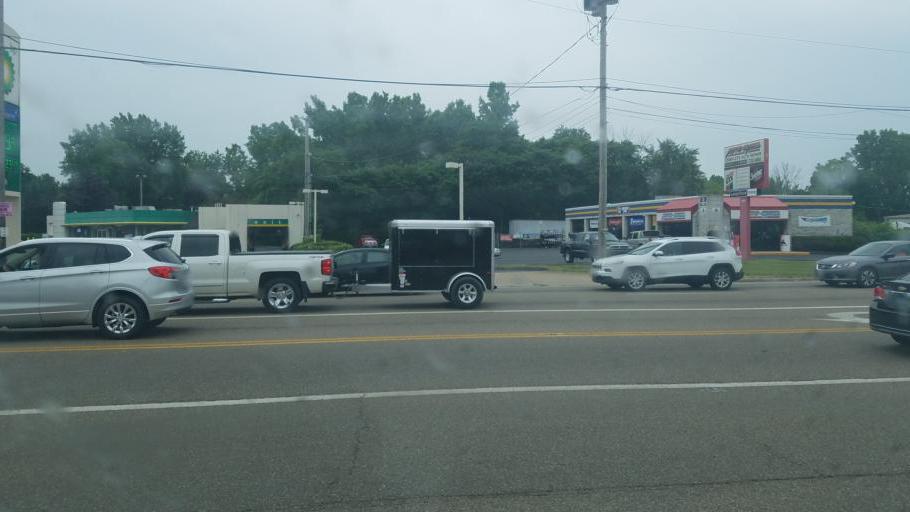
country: US
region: Ohio
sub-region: Summit County
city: Lakemore
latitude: 41.0315
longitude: -81.4282
